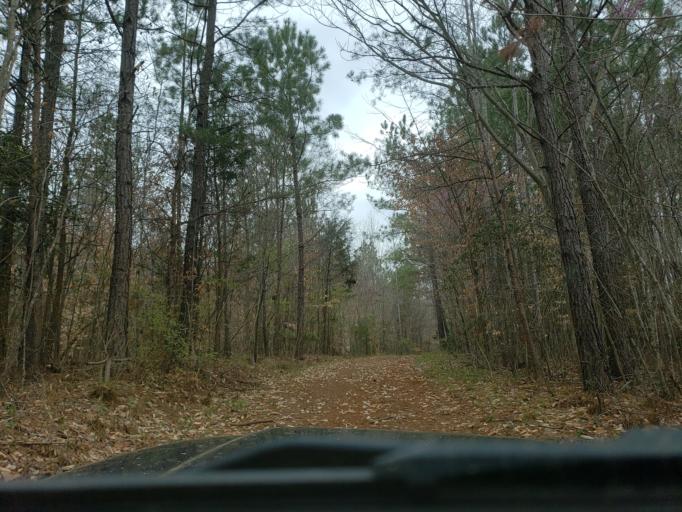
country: US
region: North Carolina
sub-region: Cleveland County
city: White Plains
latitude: 35.1870
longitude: -81.3692
